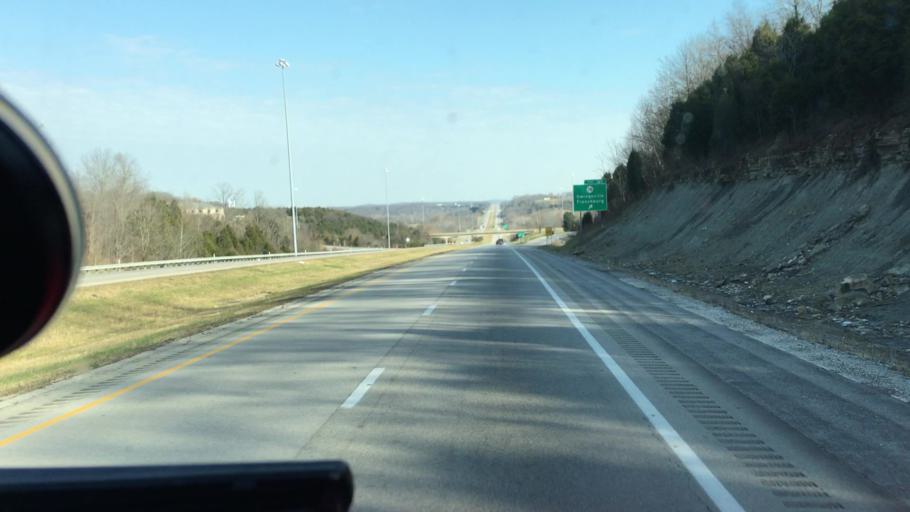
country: US
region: Kentucky
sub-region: Bath County
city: Owingsville
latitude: 38.1242
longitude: -83.7575
